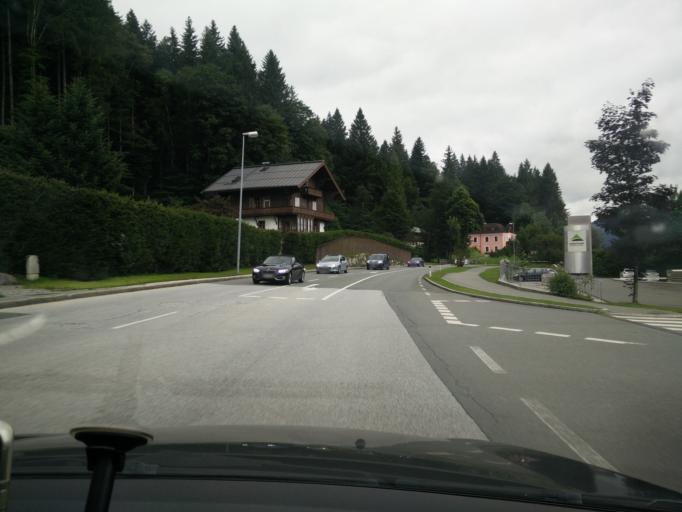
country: AT
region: Tyrol
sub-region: Politischer Bezirk Kitzbuhel
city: Kitzbuhel
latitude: 47.4510
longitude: 12.3735
